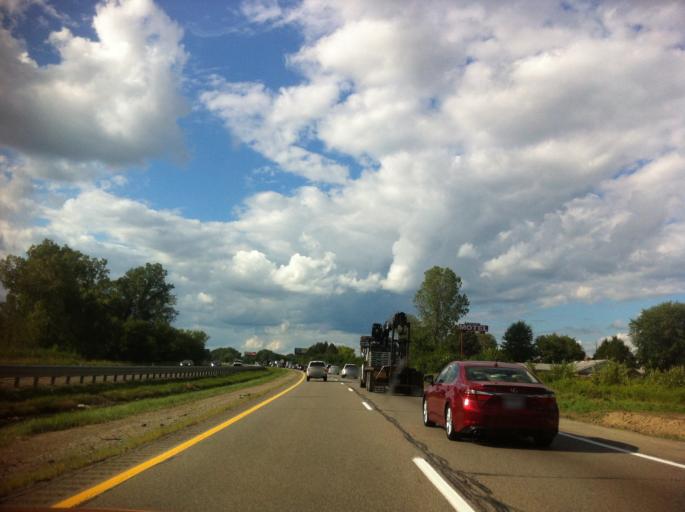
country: US
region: Michigan
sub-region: Livingston County
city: Whitmore Lake
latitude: 42.4059
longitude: -83.7626
